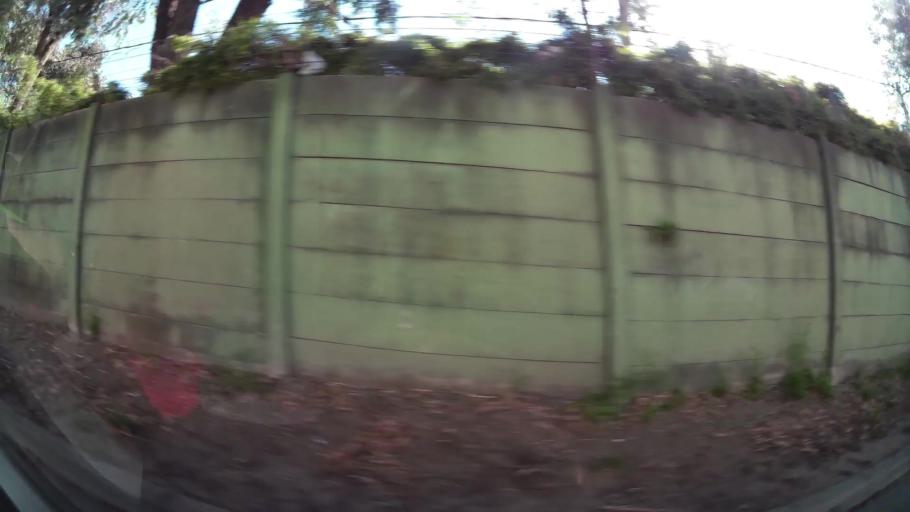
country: AR
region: Buenos Aires
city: Santa Catalina - Dique Lujan
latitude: -34.4724
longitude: -58.6799
